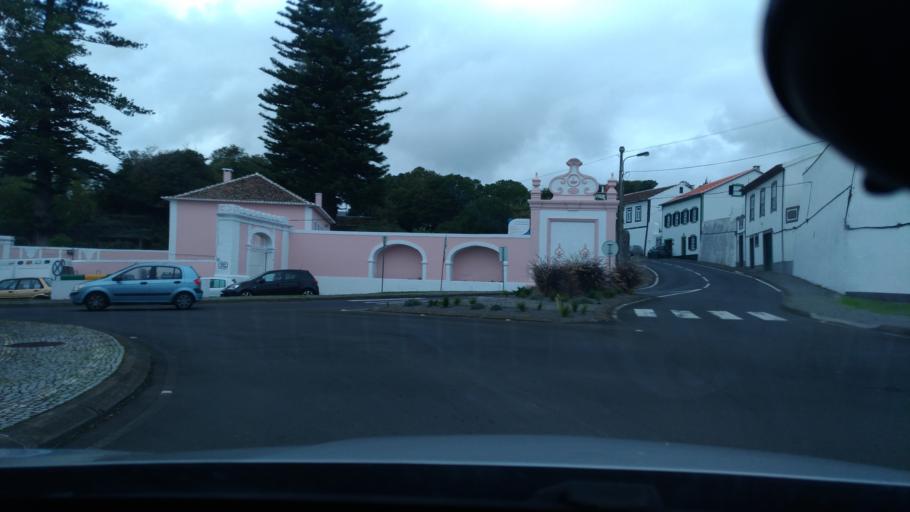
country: PT
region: Azores
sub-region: Angra do Heroismo
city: Angra do Heroismo
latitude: 38.6575
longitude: -27.2305
